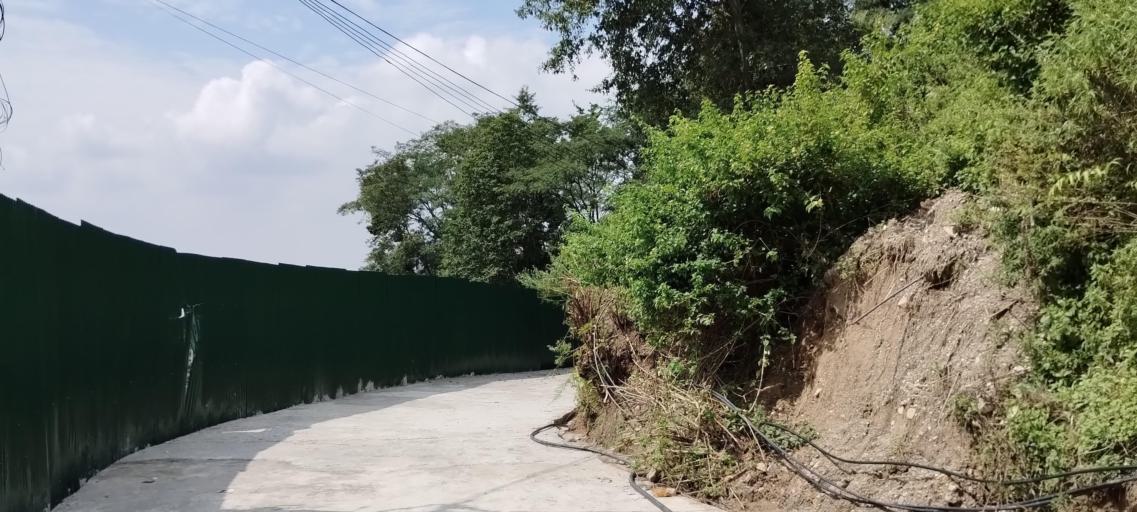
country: NP
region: Central Region
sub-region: Bagmati Zone
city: Kathmandu
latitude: 27.7897
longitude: 85.3636
